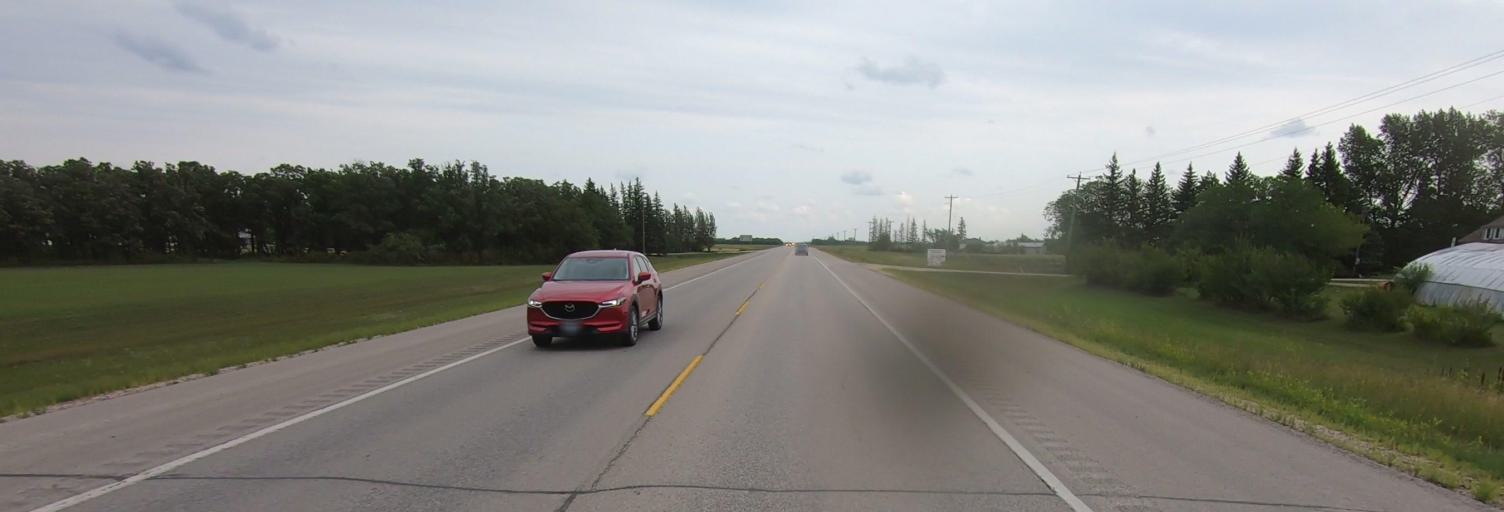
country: CA
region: Manitoba
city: Headingley
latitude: 49.7835
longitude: -97.2983
